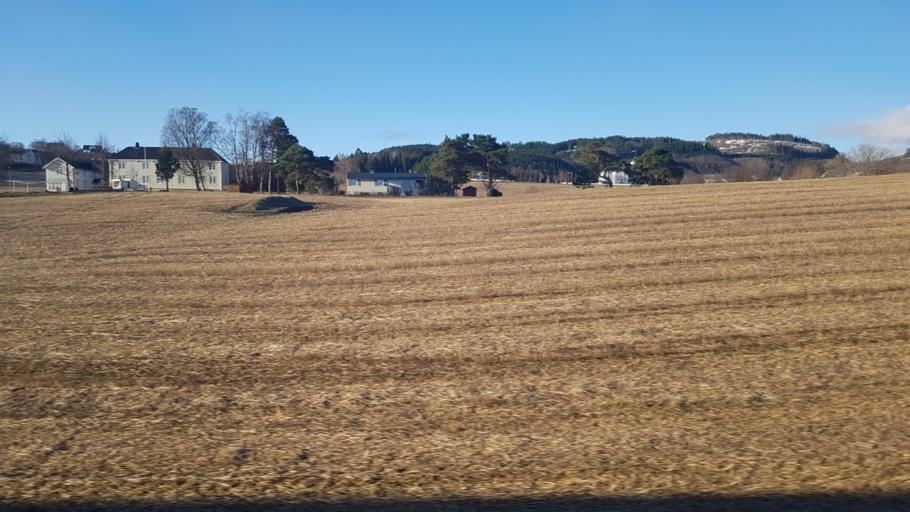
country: NO
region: Sor-Trondelag
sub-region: Malvik
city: Malvik
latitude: 63.4307
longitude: 10.6970
